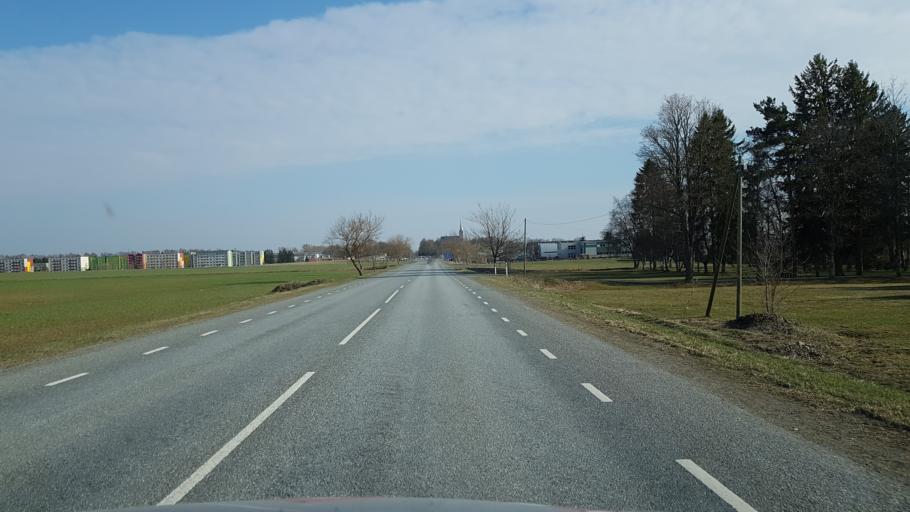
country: EE
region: Laeaene-Virumaa
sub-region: Kadrina vald
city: Kadrina
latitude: 59.3501
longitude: 26.1222
